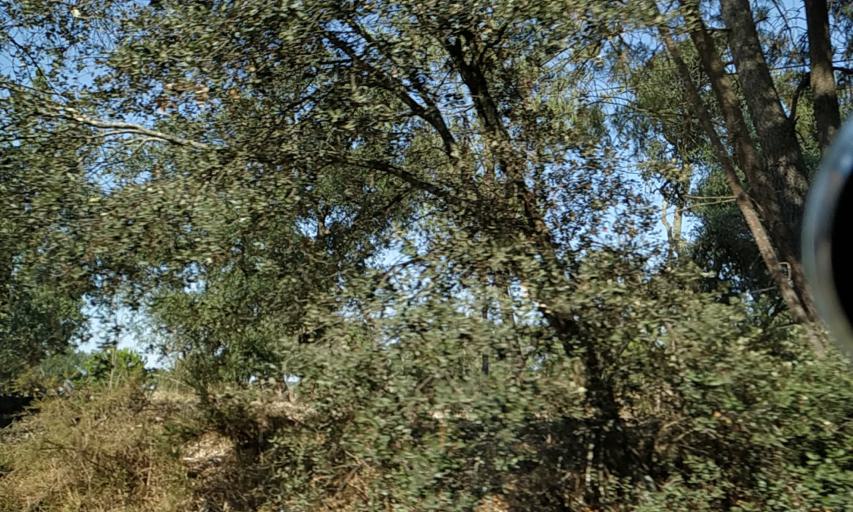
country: PT
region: Santarem
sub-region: Benavente
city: Poceirao
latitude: 38.7483
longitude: -8.6316
